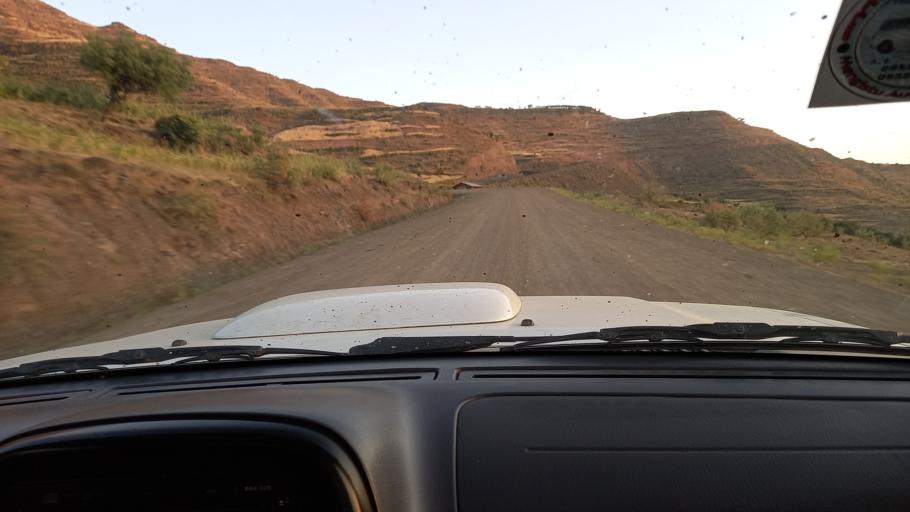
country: ET
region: Amhara
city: Debark'
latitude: 13.0544
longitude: 38.0186
